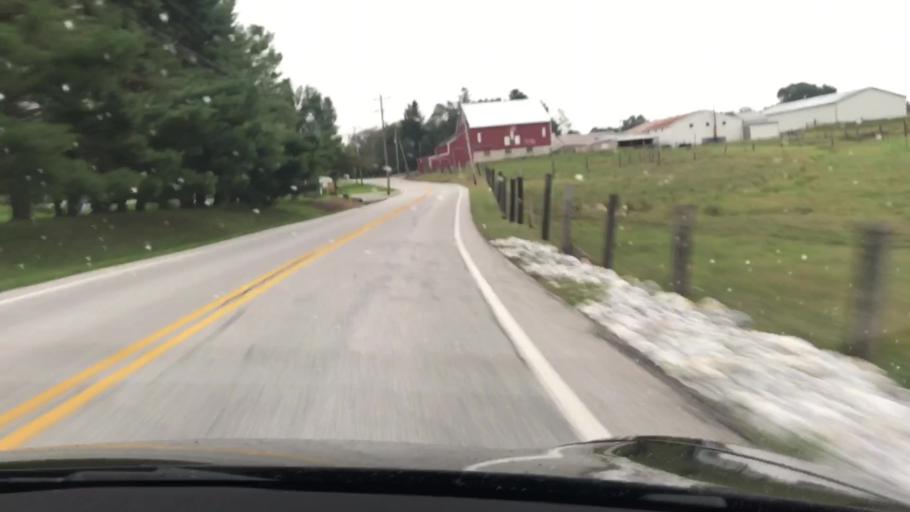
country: US
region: Pennsylvania
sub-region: York County
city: Dover
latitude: 39.9803
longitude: -76.8772
